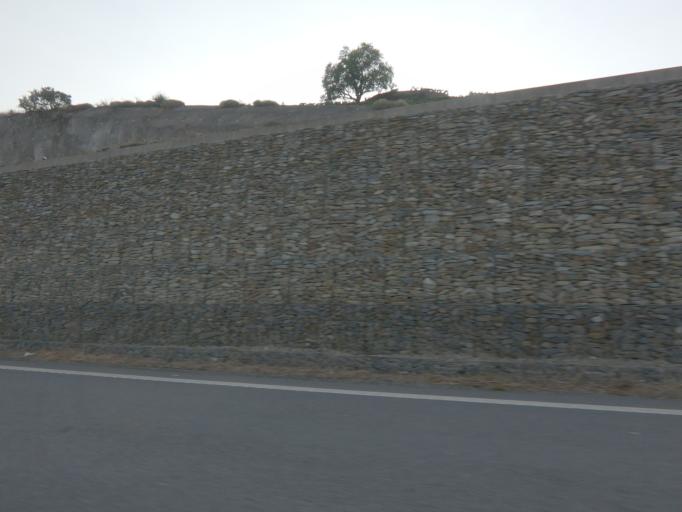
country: PT
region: Vila Real
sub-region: Peso da Regua
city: Peso da Regua
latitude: 41.1856
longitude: -7.7490
